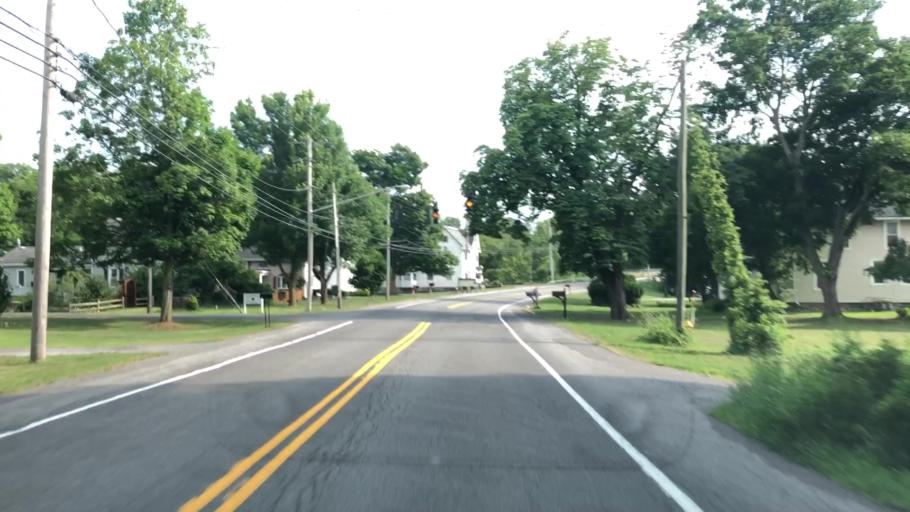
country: US
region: New York
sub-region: Erie County
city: Elma Center
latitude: 42.8501
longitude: -78.6403
